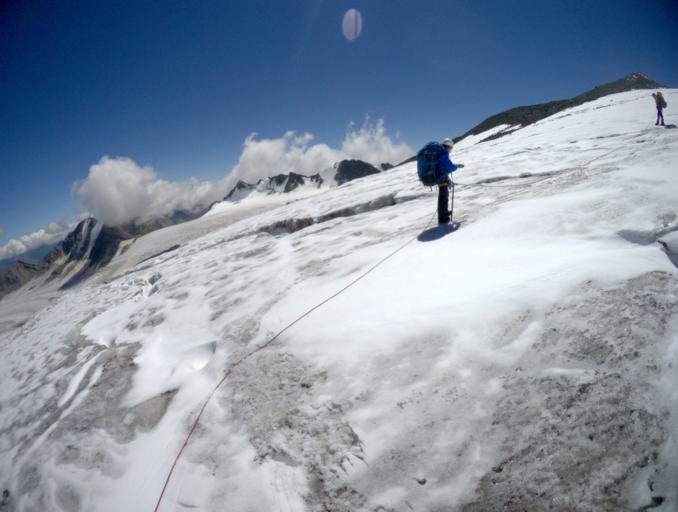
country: RU
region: Kabardino-Balkariya
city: Terskol
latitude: 43.3509
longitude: 42.5044
